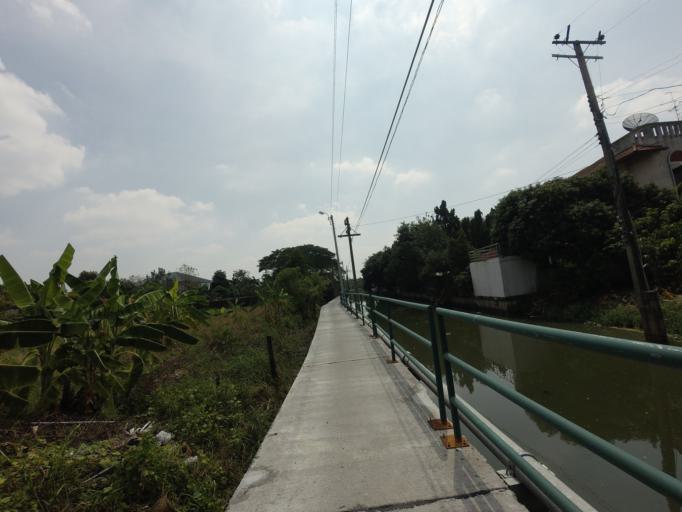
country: TH
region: Bangkok
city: Bueng Kum
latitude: 13.7685
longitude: 100.6680
